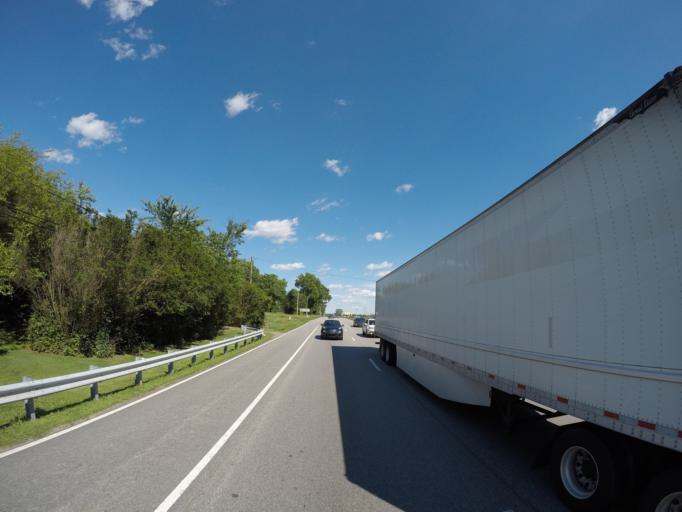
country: US
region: Maryland
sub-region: Queen Anne's County
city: Centreville
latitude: 38.9610
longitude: -76.0969
